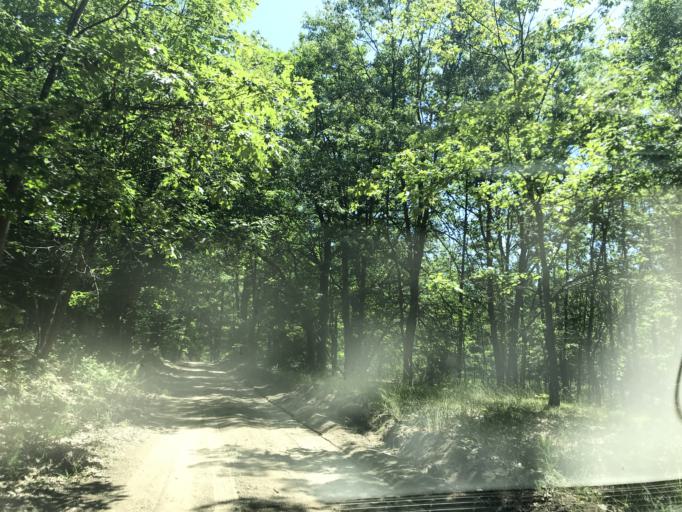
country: US
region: Michigan
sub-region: Missaukee County
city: Lake City
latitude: 44.2790
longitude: -85.0398
